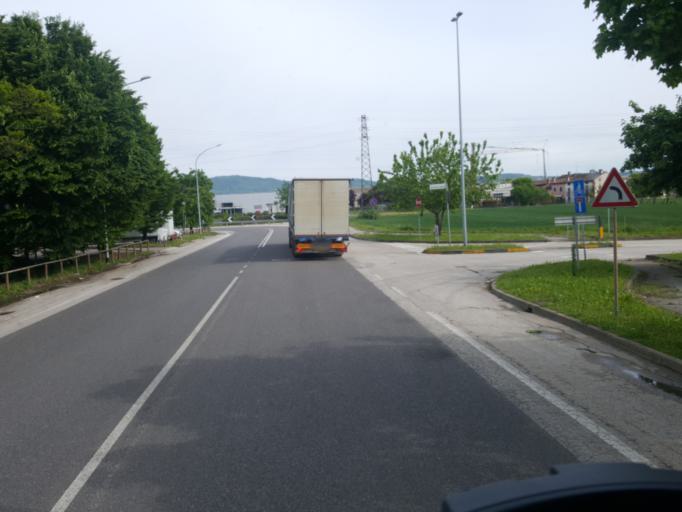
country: IT
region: Veneto
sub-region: Provincia di Vicenza
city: Montecchio Maggiore-Alte Ceccato
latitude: 45.4879
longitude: 11.4129
